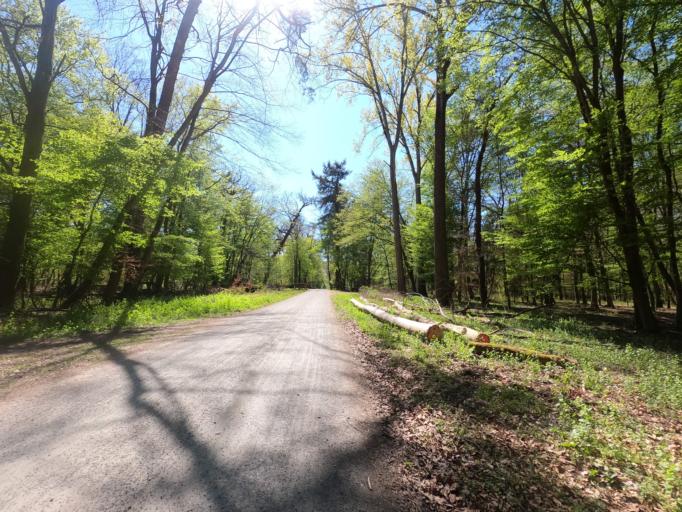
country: DE
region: Hesse
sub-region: Regierungsbezirk Darmstadt
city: Gross-Gerau
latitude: 49.9510
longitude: 8.5009
